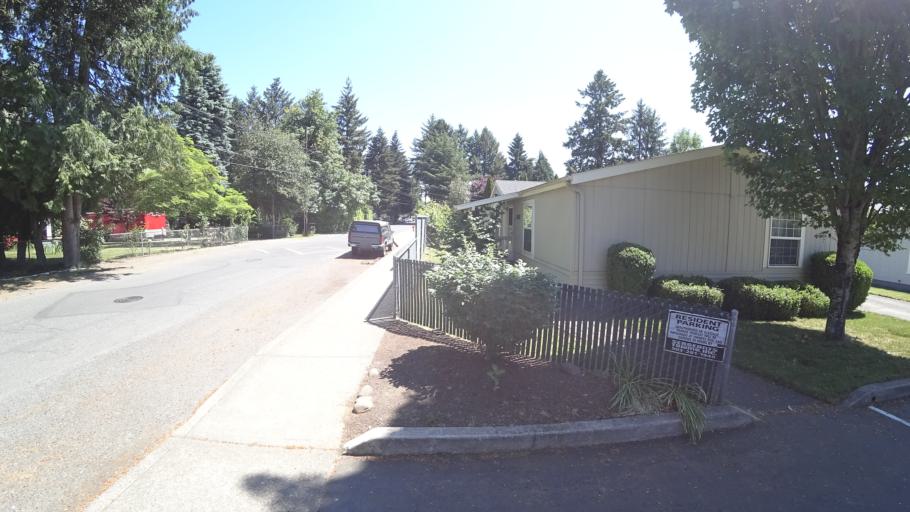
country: US
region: Oregon
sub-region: Clackamas County
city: Happy Valley
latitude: 45.4800
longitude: -122.5309
